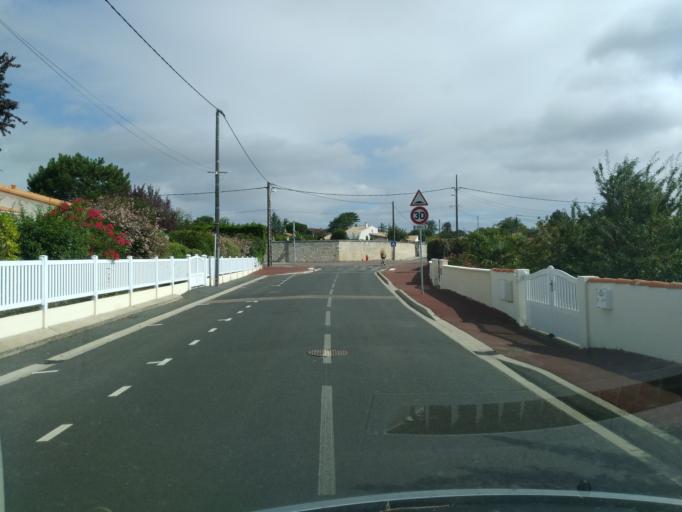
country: FR
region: Poitou-Charentes
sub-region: Departement de la Charente-Maritime
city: Saint-Palais-sur-Mer
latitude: 45.6504
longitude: -1.0769
